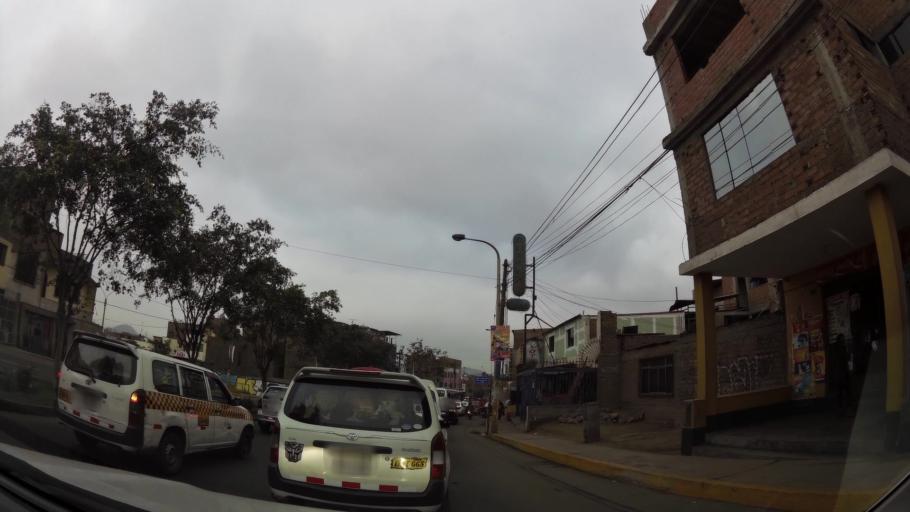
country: PE
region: Lima
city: Lima
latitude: -12.0240
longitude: -77.0122
